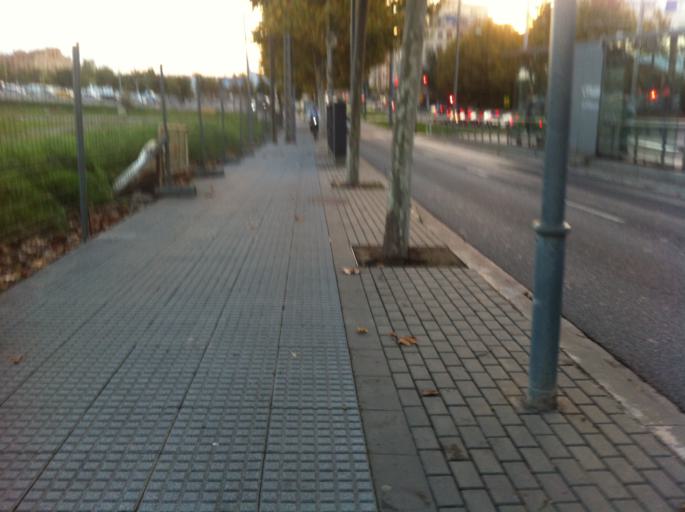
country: ES
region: Catalonia
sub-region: Provincia de Barcelona
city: Esplugues de Llobregat
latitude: 41.3768
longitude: 2.0982
